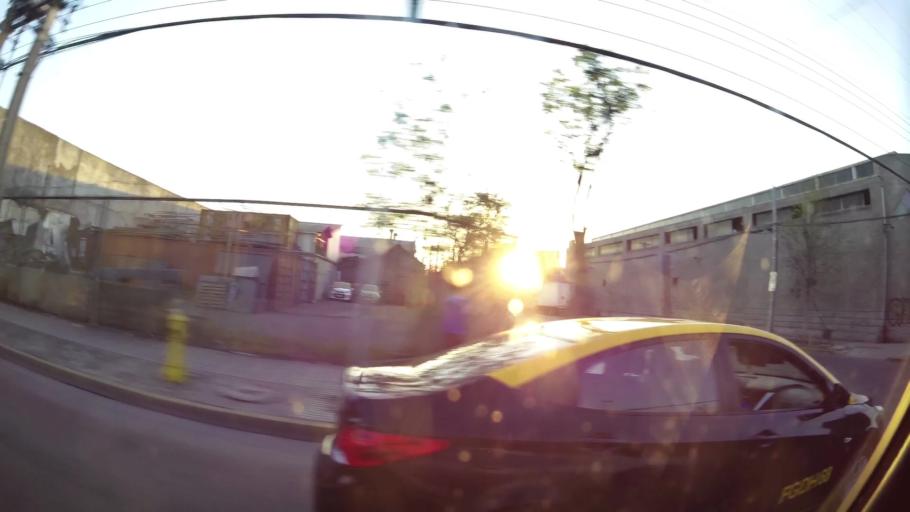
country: CL
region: Santiago Metropolitan
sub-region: Provincia de Santiago
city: Santiago
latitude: -33.4603
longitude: -70.6732
